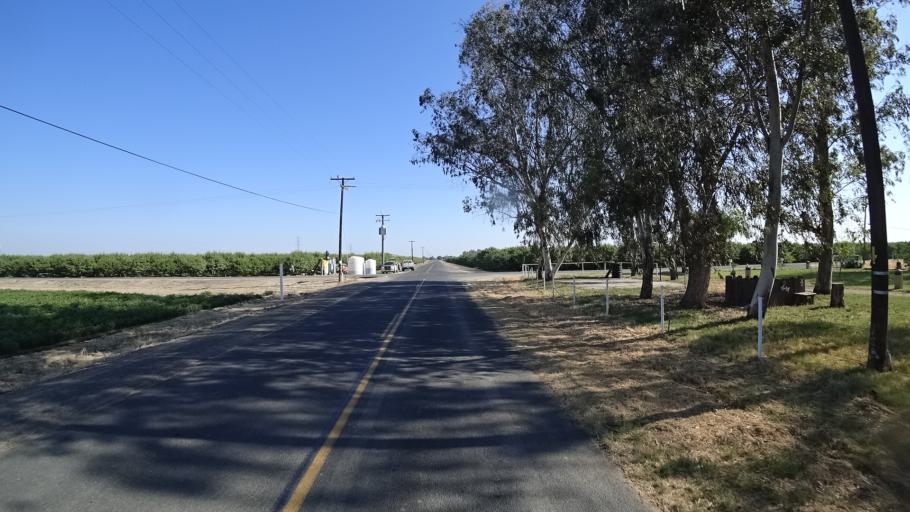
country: US
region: California
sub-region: Fresno County
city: Riverdale
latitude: 36.3652
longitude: -119.8872
